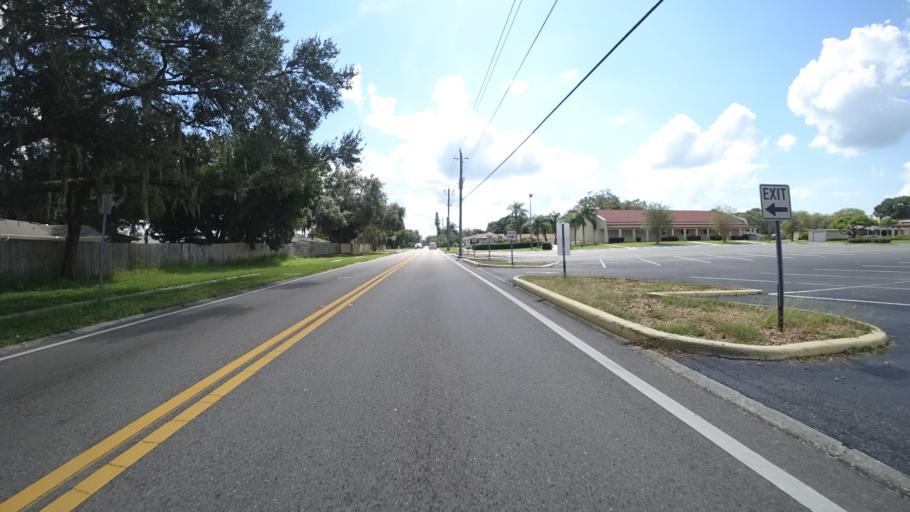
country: US
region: Florida
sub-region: Manatee County
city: Whitfield
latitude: 27.4230
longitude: -82.5550
